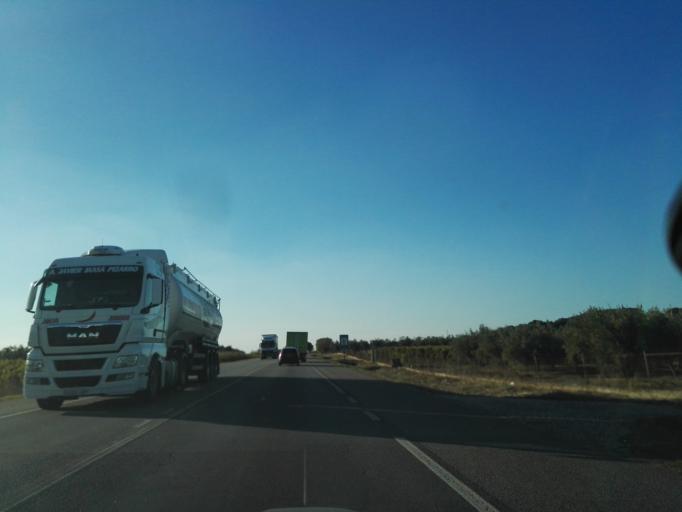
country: PT
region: Evora
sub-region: Estremoz
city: Estremoz
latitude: 38.8283
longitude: -7.5290
